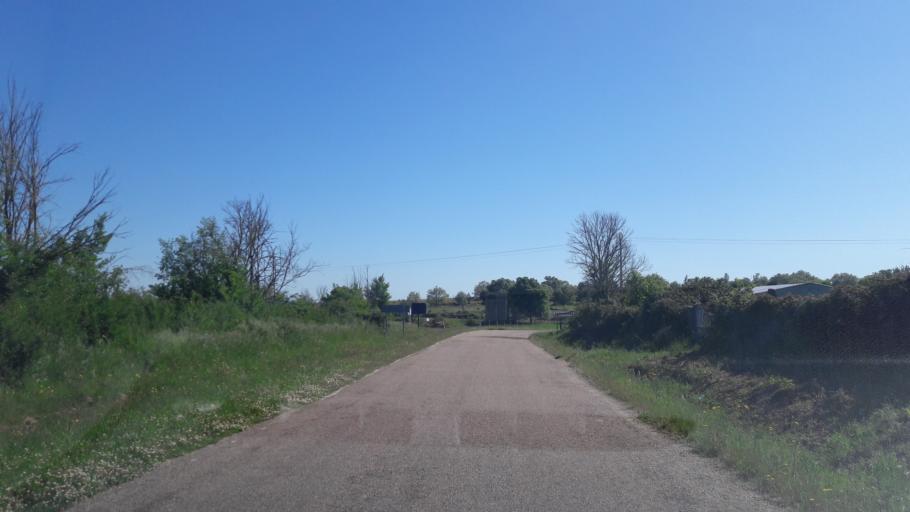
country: ES
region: Castille and Leon
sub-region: Provincia de Salamanca
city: Banobarez
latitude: 40.8520
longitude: -6.6110
